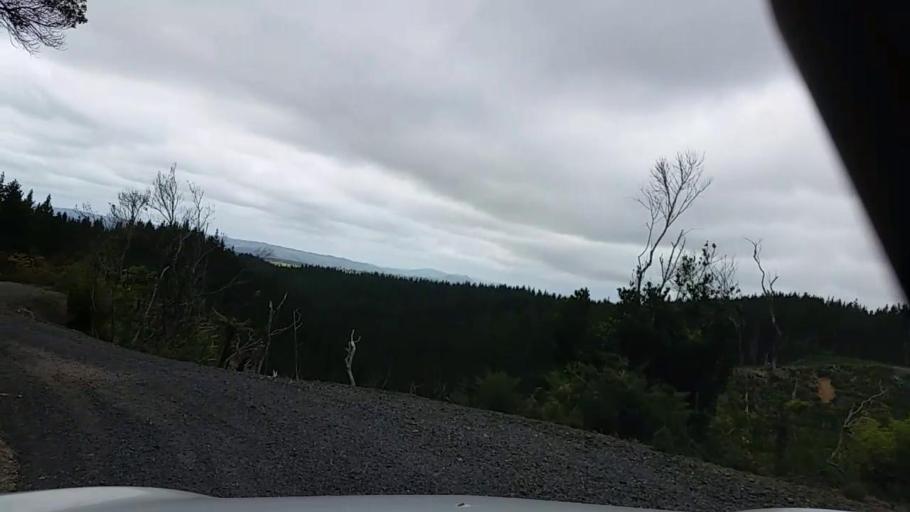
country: NZ
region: Northland
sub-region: Far North District
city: Kawakawa
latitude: -35.4604
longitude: 174.2618
